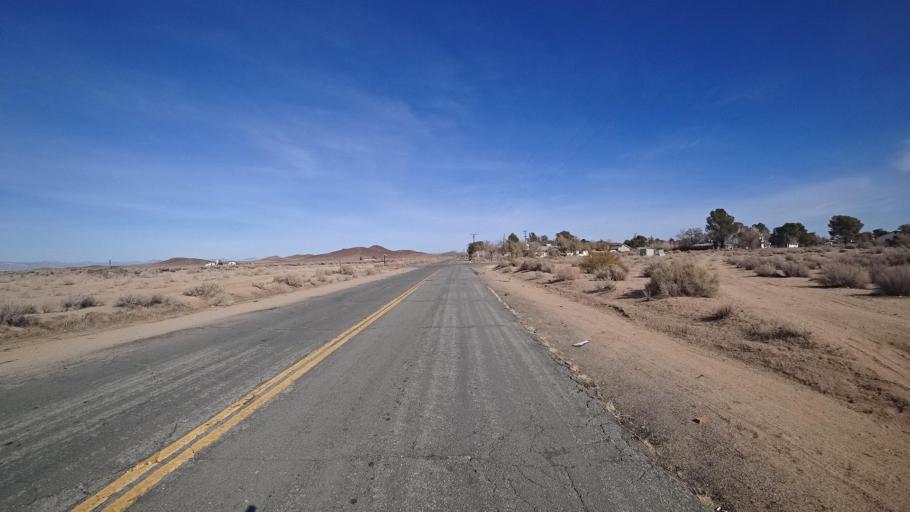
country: US
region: California
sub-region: Kern County
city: North Edwards
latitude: 35.0206
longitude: -117.8342
